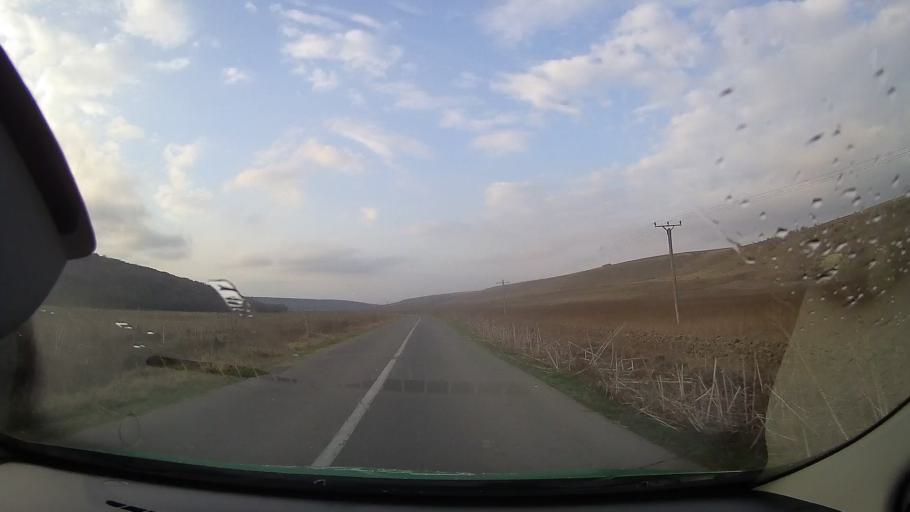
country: RO
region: Constanta
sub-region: Comuna Dobromir
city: Dobromir
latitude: 44.0249
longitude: 27.8675
